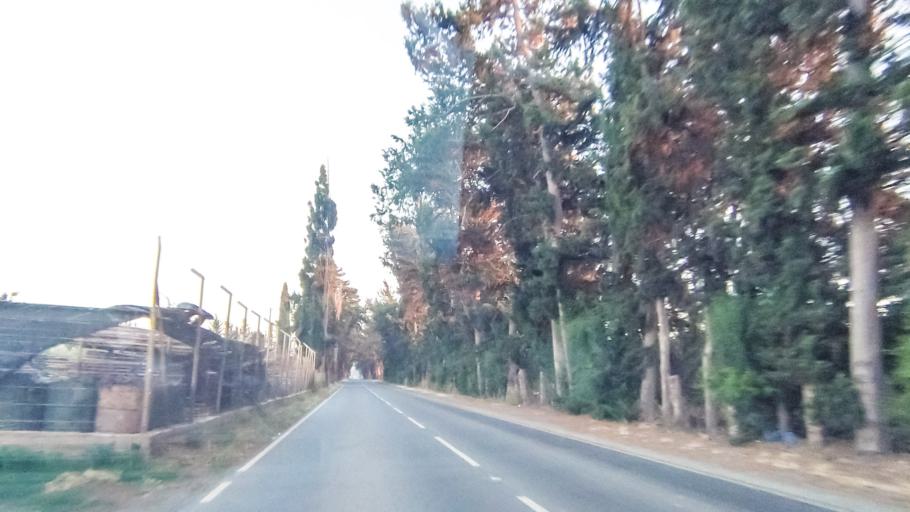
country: CY
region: Larnaka
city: Kolossi
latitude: 34.6415
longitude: 32.9451
